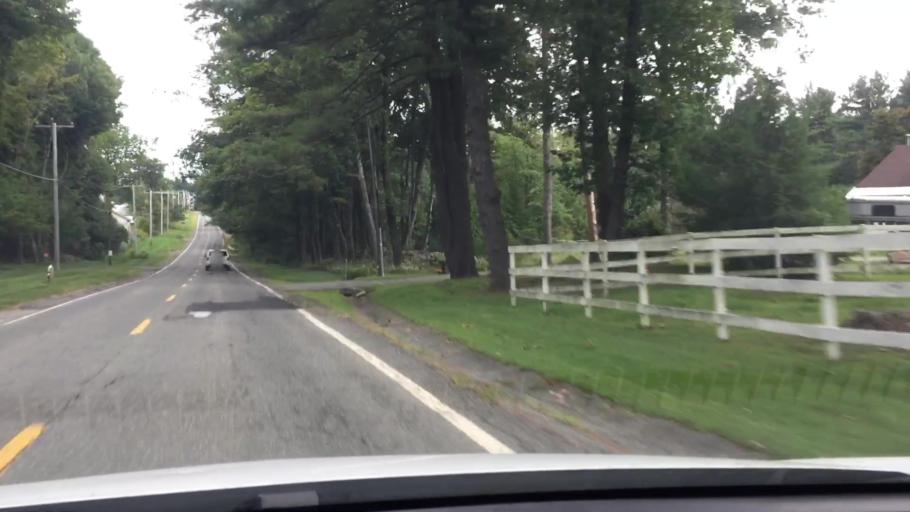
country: US
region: Massachusetts
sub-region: Hampden County
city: Granville
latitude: 42.1865
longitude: -72.9315
